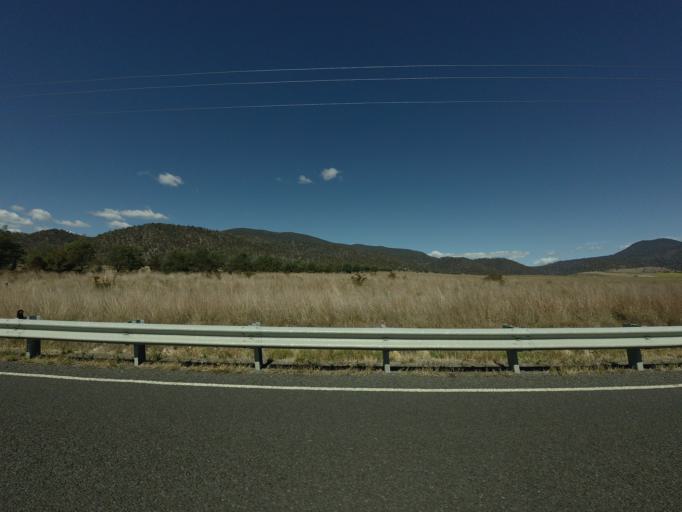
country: AU
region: Tasmania
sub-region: Break O'Day
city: St Helens
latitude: -41.7080
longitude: 147.8465
